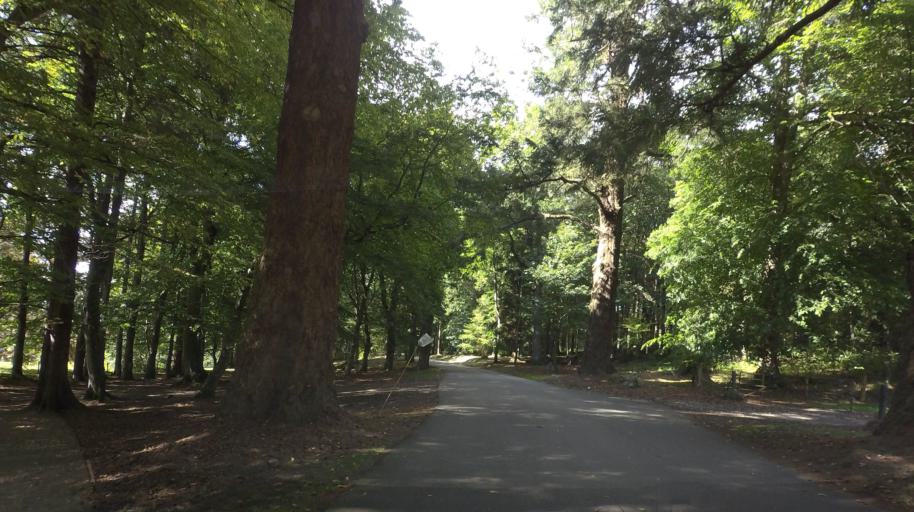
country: GB
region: Scotland
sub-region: Aberdeenshire
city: Banchory
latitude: 57.0600
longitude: -2.4357
